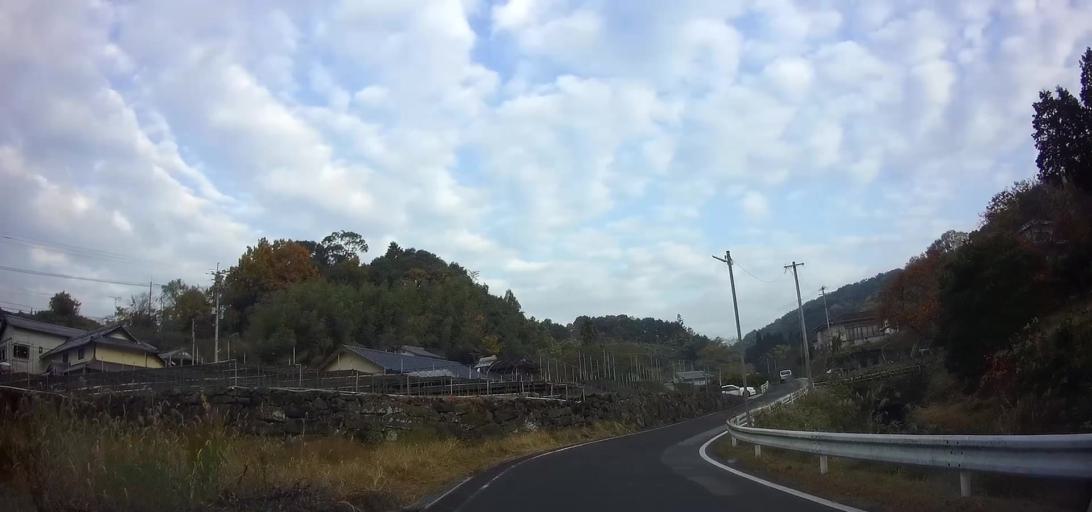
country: JP
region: Nagasaki
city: Shimabara
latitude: 32.6583
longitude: 130.2494
